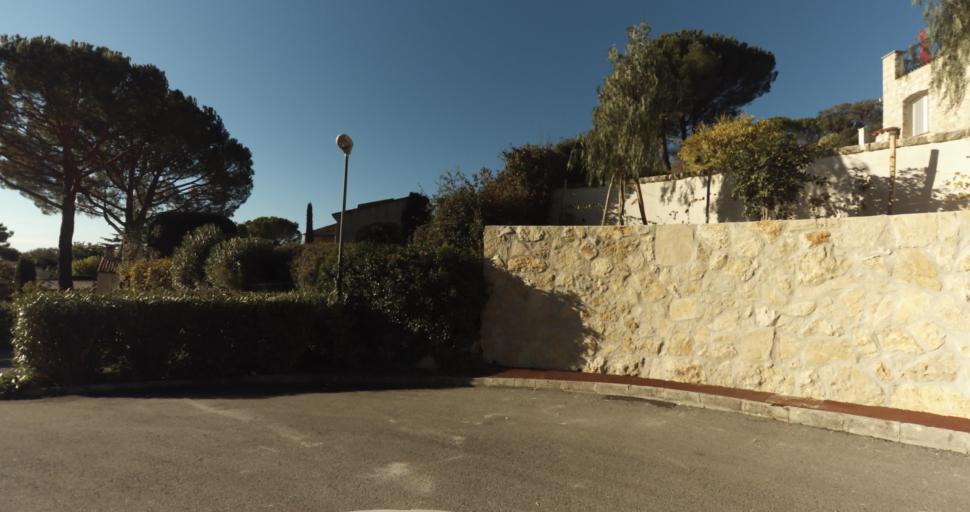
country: FR
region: Provence-Alpes-Cote d'Azur
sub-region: Departement des Alpes-Maritimes
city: Vence
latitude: 43.7261
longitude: 7.0820
